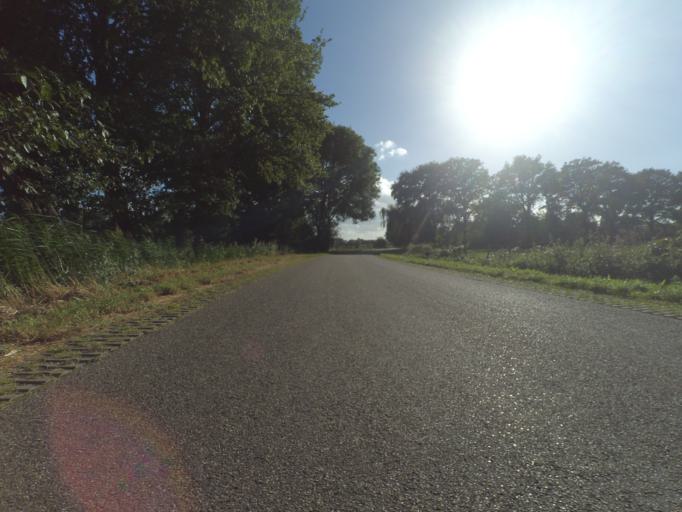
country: NL
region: Gelderland
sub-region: Gemeente Ede
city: Ederveen
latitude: 52.0902
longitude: 5.5519
